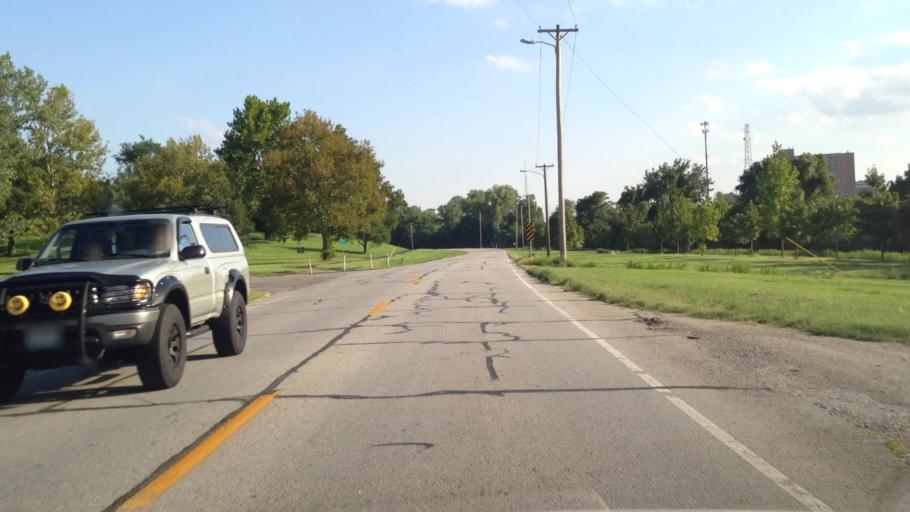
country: US
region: Missouri
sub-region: Jasper County
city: Joplin
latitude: 37.0959
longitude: -94.5109
